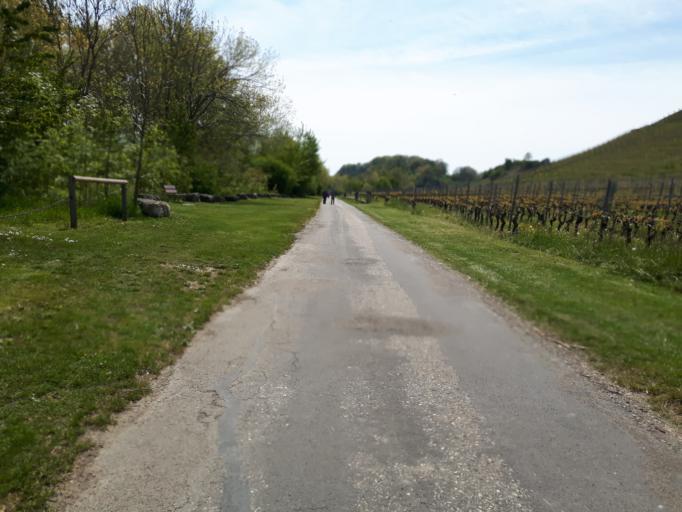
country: CH
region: Neuchatel
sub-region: Boudry District
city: Cortaillod
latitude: 46.9390
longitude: 6.8449
